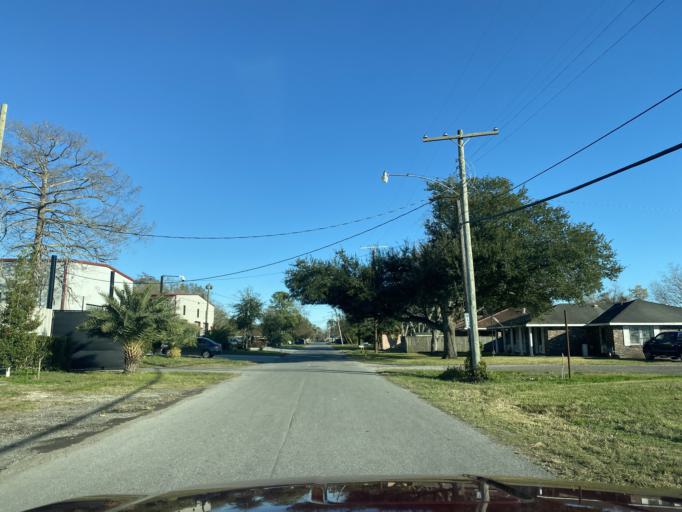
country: US
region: Louisiana
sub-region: Jefferson Parish
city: Kenner
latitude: 29.9904
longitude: -90.2469
